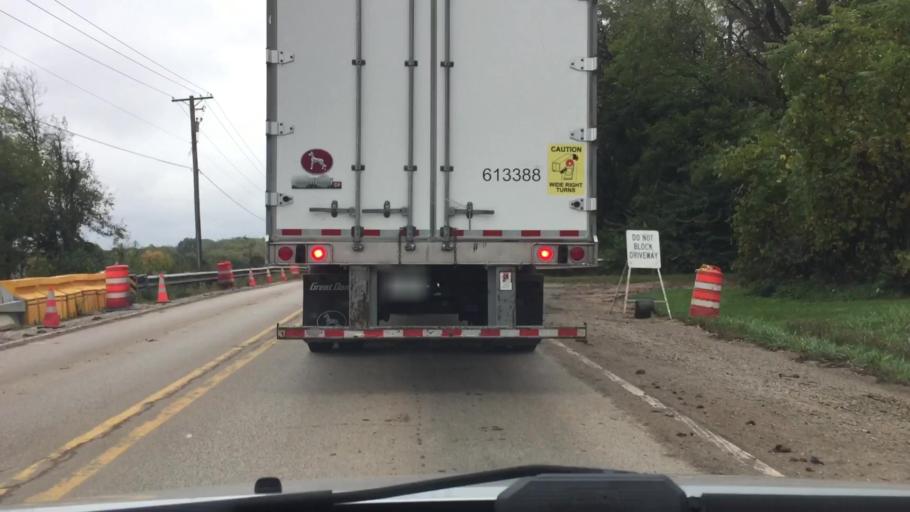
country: US
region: Illinois
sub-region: Kane County
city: Sleepy Hollow
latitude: 42.1271
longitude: -88.3009
